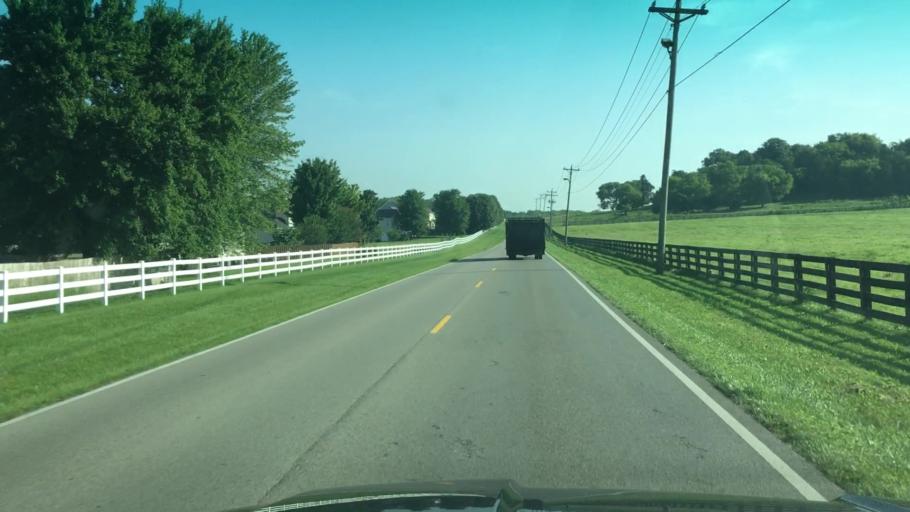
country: US
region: Tennessee
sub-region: Williamson County
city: Thompson's Station
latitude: 35.7856
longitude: -86.8783
